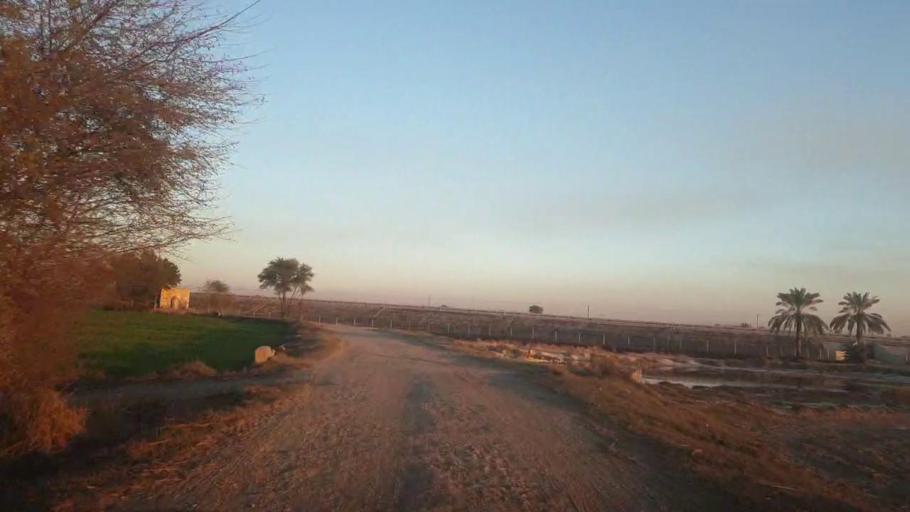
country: PK
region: Sindh
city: Ghotki
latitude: 28.0332
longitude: 69.3082
